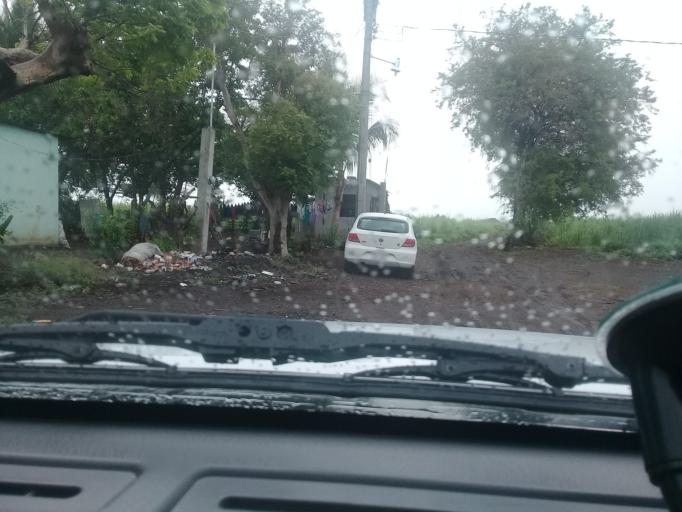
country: MX
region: Veracruz
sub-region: Puente Nacional
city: Cabezas
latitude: 19.3457
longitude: -96.3937
